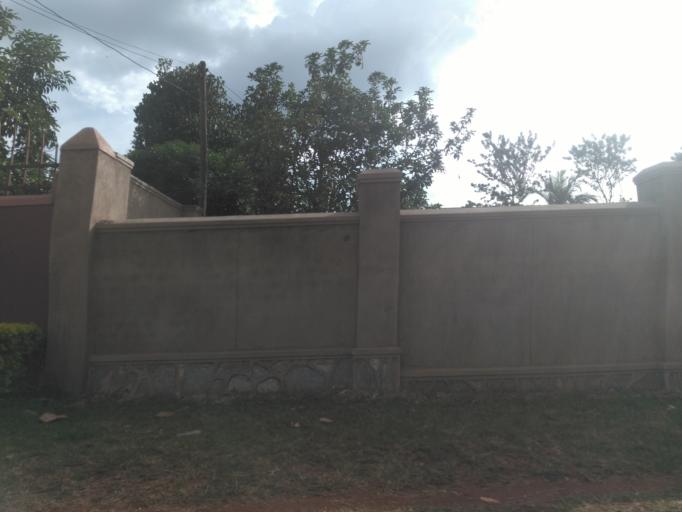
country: UG
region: Eastern Region
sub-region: Jinja District
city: Jinja
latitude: 0.4267
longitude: 33.2053
